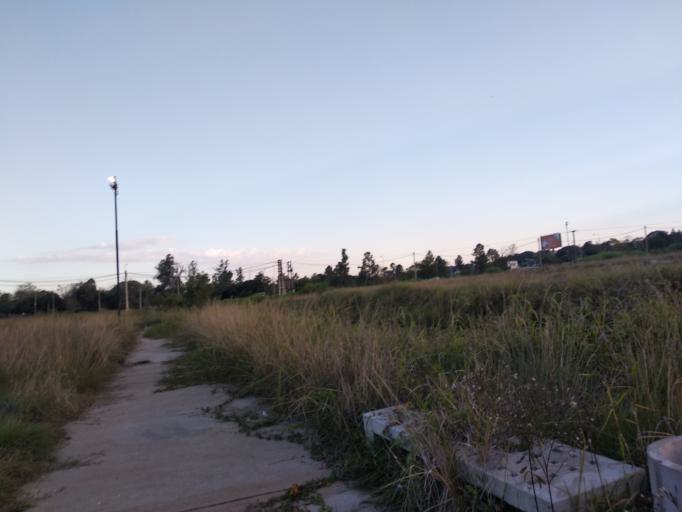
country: AR
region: Misiones
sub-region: Departamento de Capital
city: Posadas
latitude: -27.3969
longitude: -55.9560
